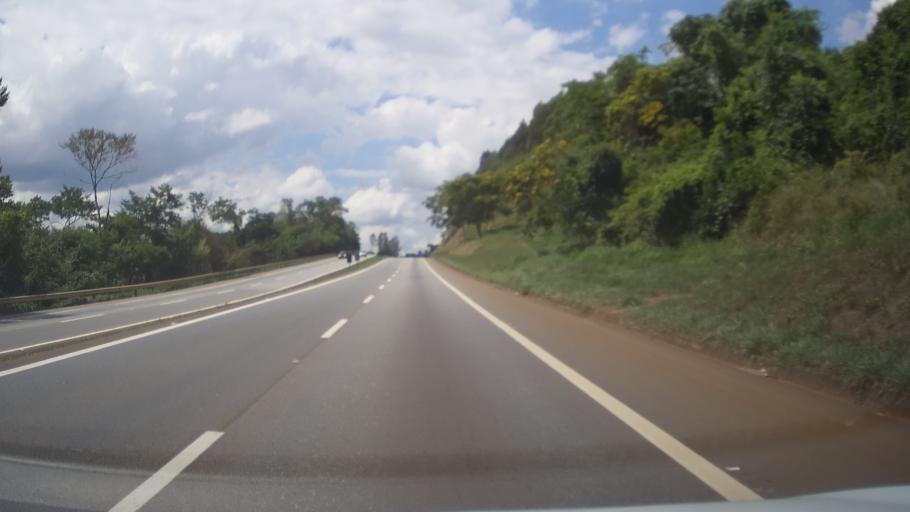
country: BR
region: Minas Gerais
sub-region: Nepomuceno
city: Nepomuceno
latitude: -21.2964
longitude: -45.1498
